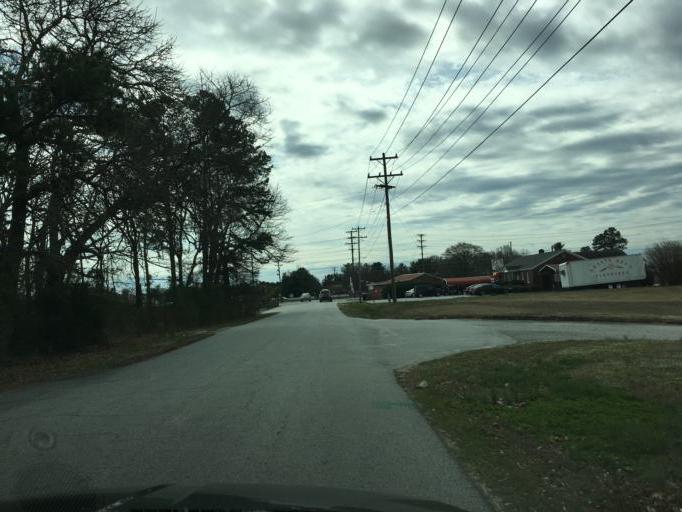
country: US
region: South Carolina
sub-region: Greenville County
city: Fountain Inn
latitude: 34.6923
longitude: -82.2216
